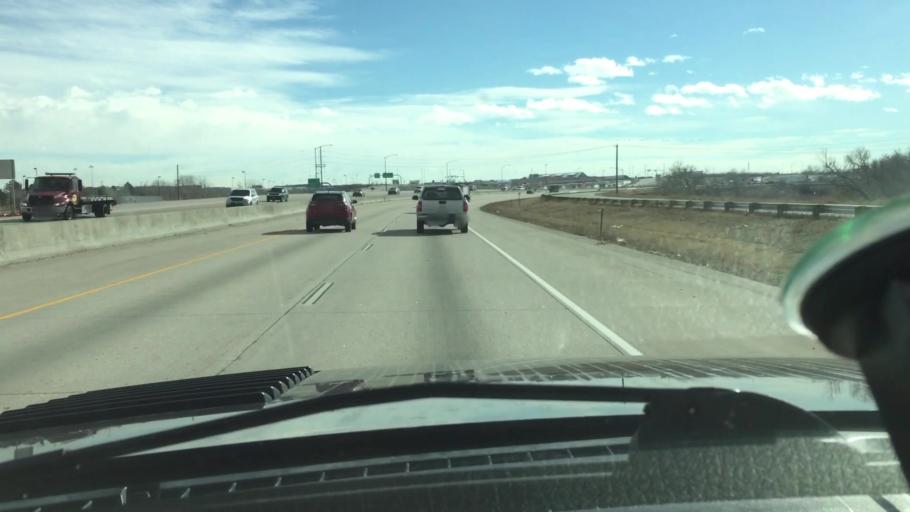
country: US
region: Colorado
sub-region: Adams County
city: Commerce City
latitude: 39.7890
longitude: -104.9062
